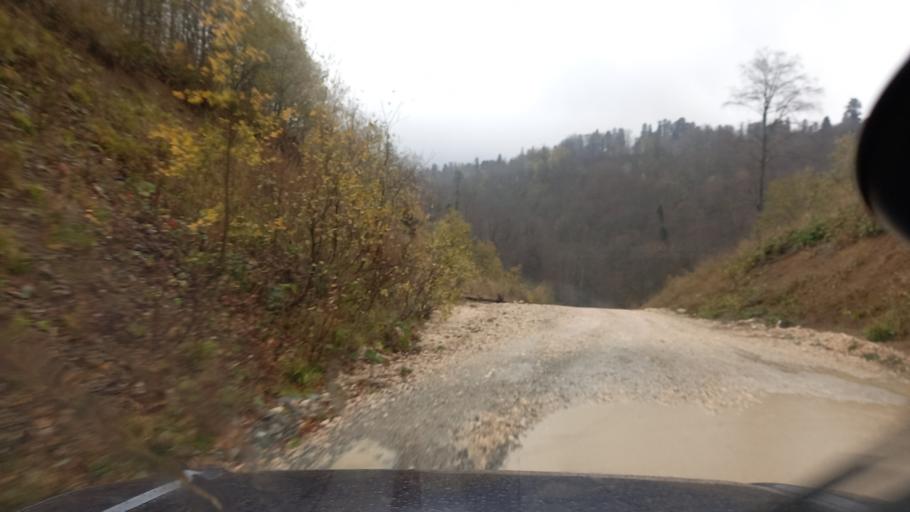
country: RU
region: Krasnodarskiy
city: Dagomys
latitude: 43.9851
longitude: 39.8502
